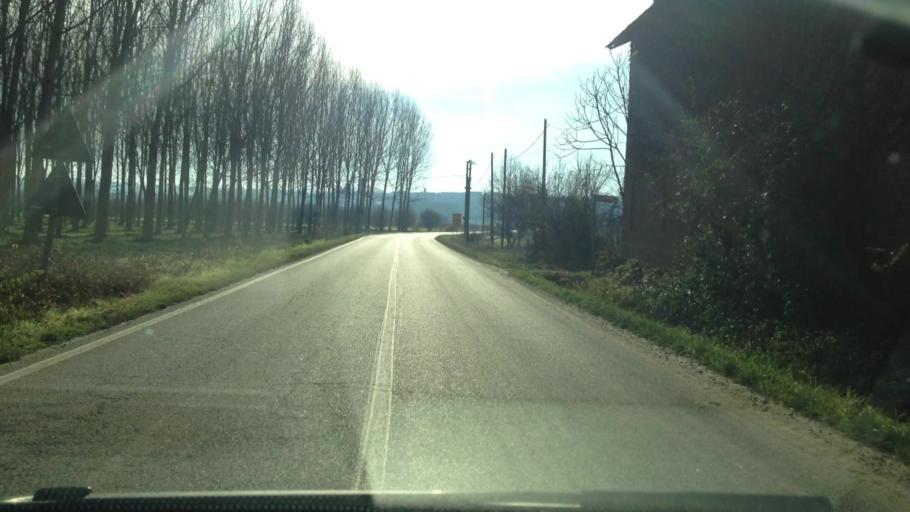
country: IT
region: Piedmont
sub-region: Provincia di Alessandria
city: Masio
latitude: 44.8839
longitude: 8.4103
